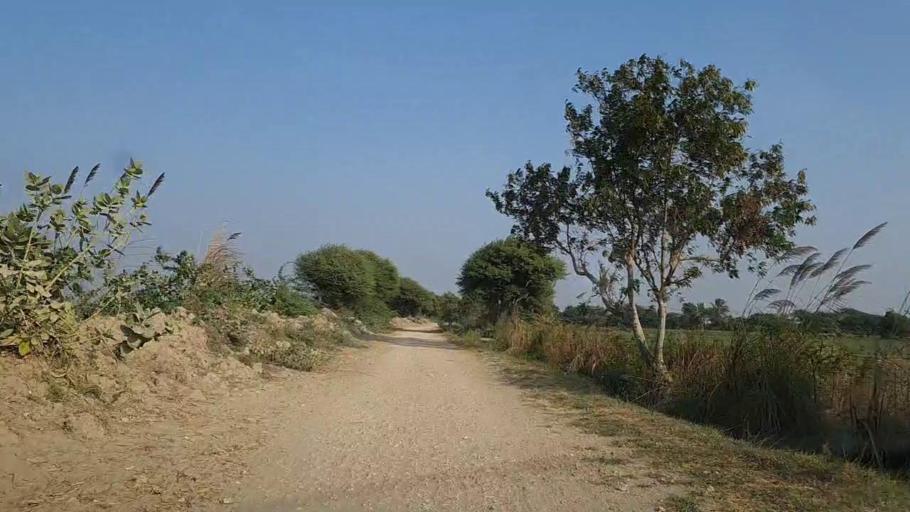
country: PK
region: Sindh
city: Mirpur Sakro
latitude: 24.5998
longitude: 67.6524
